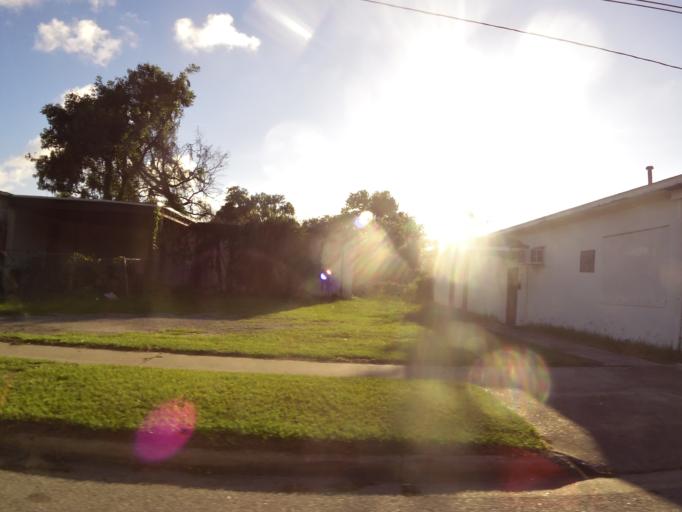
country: US
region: Georgia
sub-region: Glynn County
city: Brunswick
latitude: 31.1519
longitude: -81.4885
